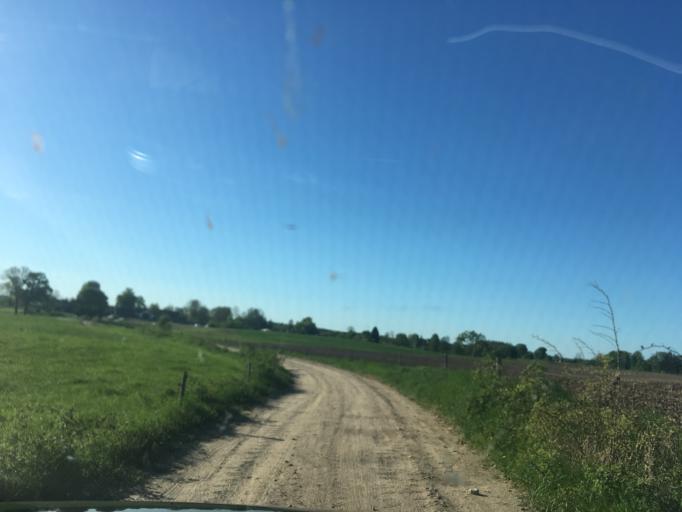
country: PL
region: Warmian-Masurian Voivodeship
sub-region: Powiat piski
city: Ruciane-Nida
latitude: 53.6596
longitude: 21.4819
